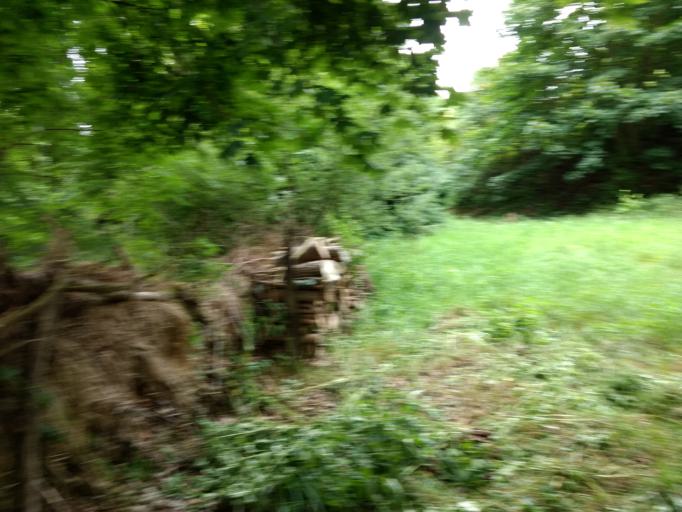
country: BE
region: Flanders
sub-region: Provincie Vlaams-Brabant
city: Oud-Heverlee
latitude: 50.8370
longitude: 4.6546
